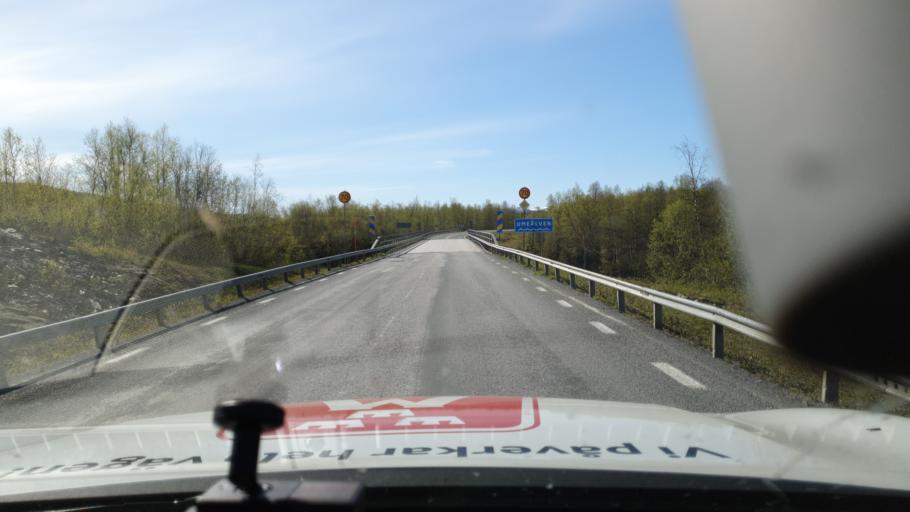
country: NO
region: Nordland
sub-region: Rana
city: Mo i Rana
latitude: 65.7822
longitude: 15.1109
